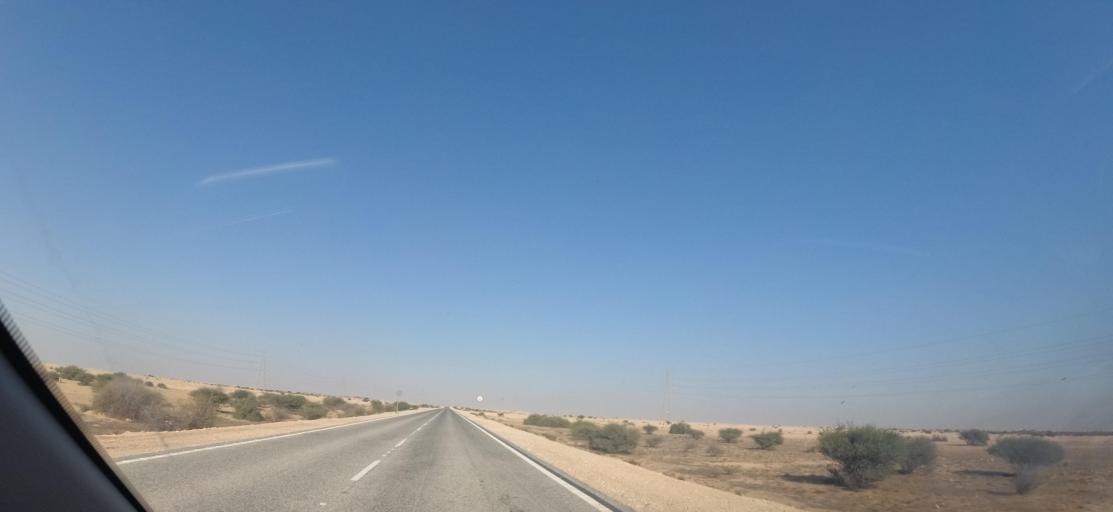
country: QA
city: Al Jumayliyah
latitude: 25.6426
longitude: 51.1052
